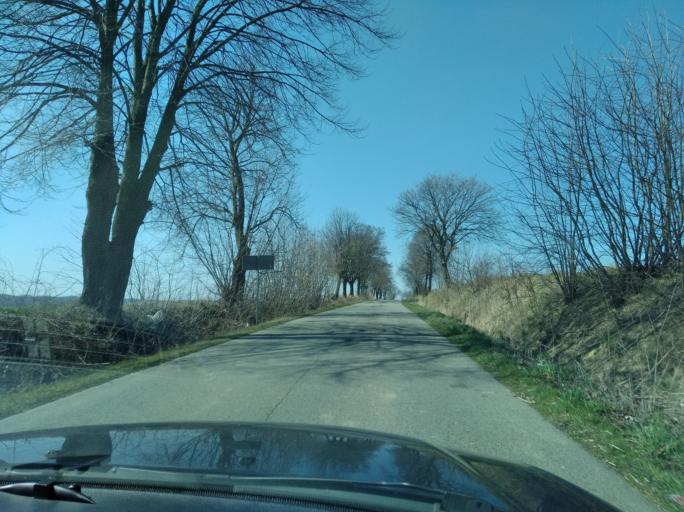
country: PL
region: Subcarpathian Voivodeship
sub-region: Powiat jaroslawski
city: Jodlowka
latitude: 49.9266
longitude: 22.4748
